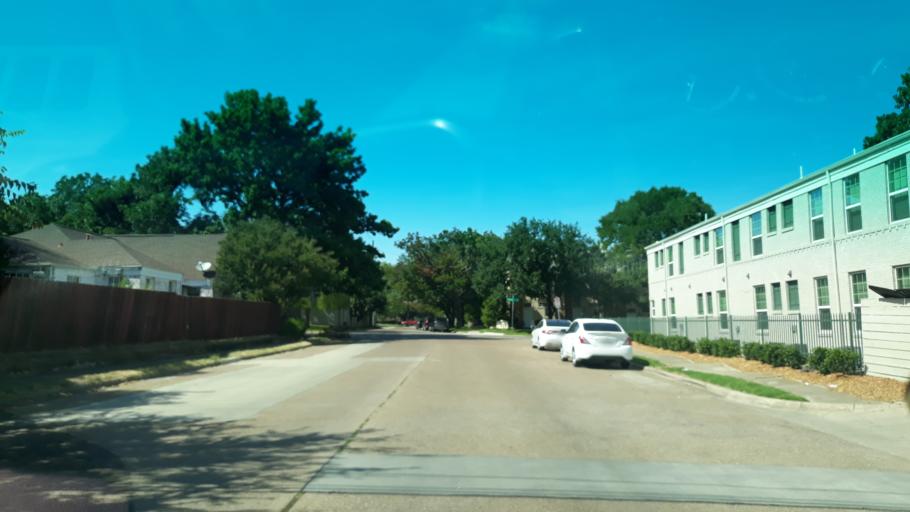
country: US
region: Texas
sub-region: Dallas County
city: Highland Park
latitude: 32.8144
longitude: -96.7551
